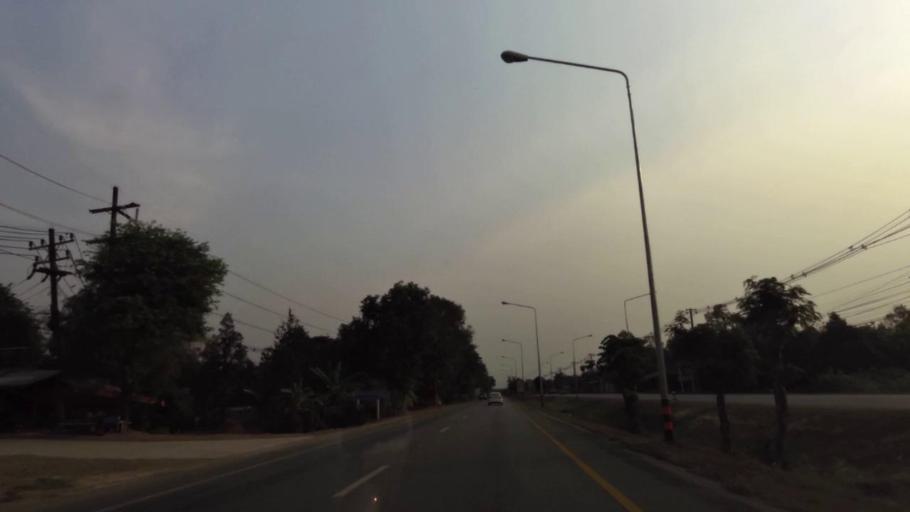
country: TH
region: Chanthaburi
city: Khlung
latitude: 12.5063
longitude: 102.1698
